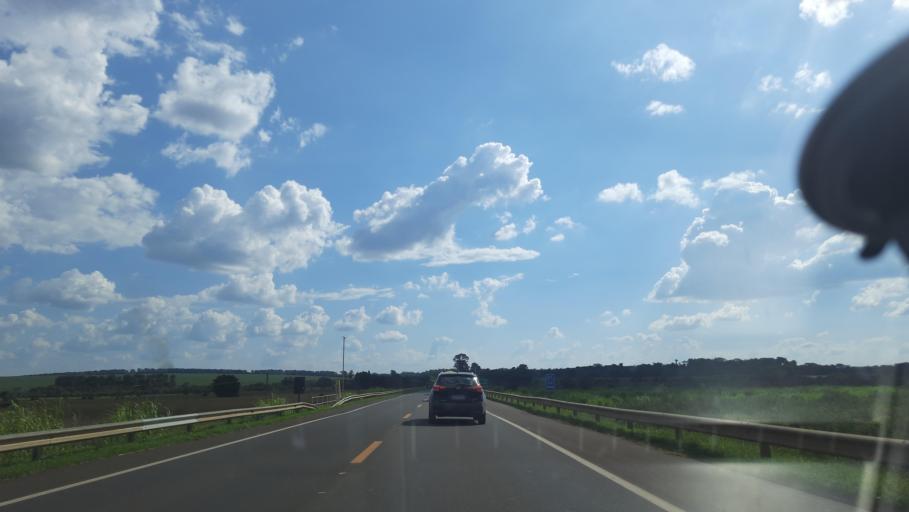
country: BR
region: Sao Paulo
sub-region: Casa Branca
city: Casa Branca
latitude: -21.7460
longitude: -46.9866
